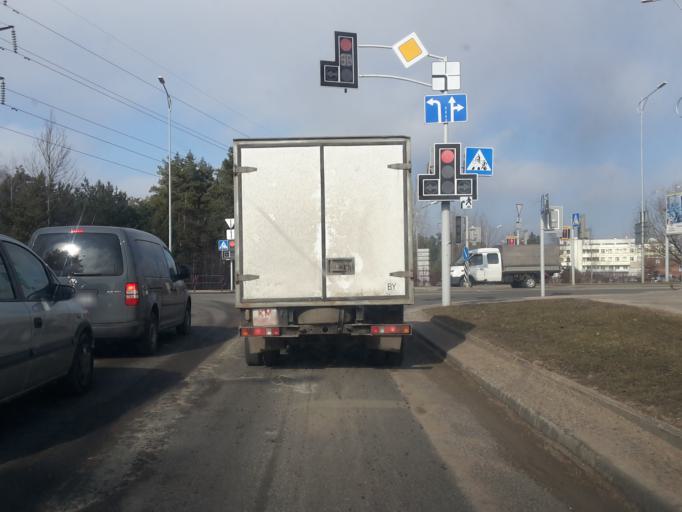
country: BY
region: Minsk
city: Borovlyany
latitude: 53.9254
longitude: 27.6814
